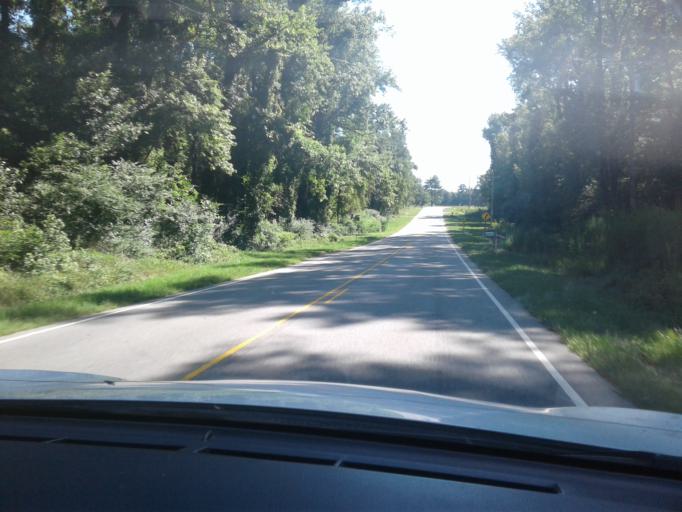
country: US
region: North Carolina
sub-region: Harnett County
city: Lillington
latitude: 35.3653
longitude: -78.8920
